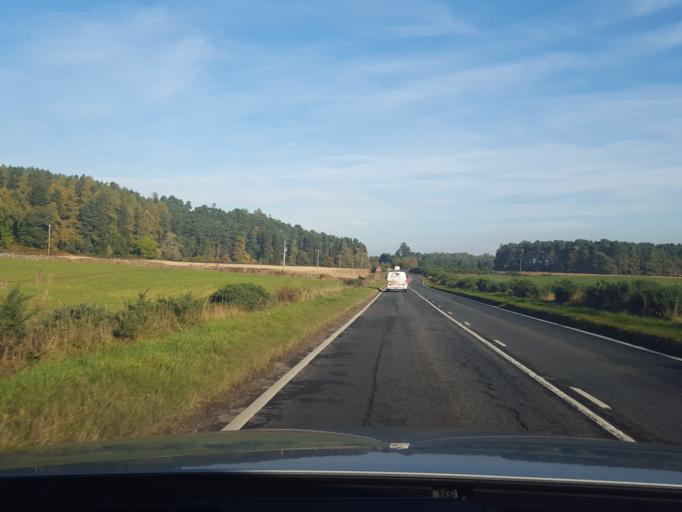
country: GB
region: Scotland
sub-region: Highland
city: Inverness
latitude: 57.4493
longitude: -4.2851
